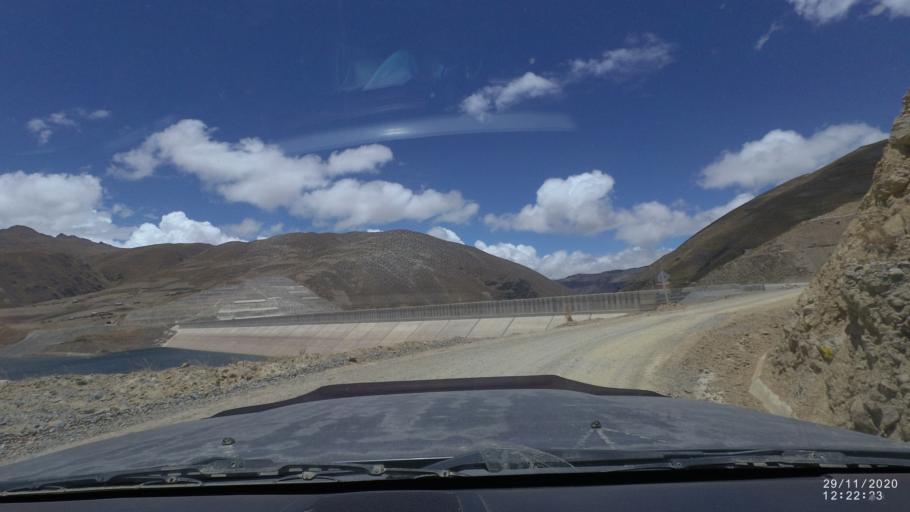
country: BO
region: Cochabamba
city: Cochabamba
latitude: -17.0974
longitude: -66.3278
